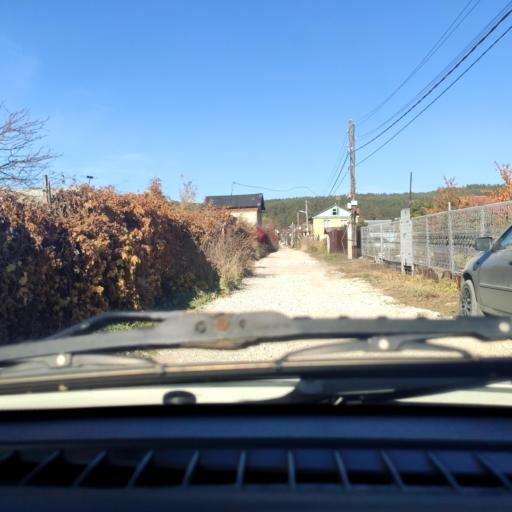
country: RU
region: Samara
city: Zhigulevsk
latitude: 53.4650
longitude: 49.5884
